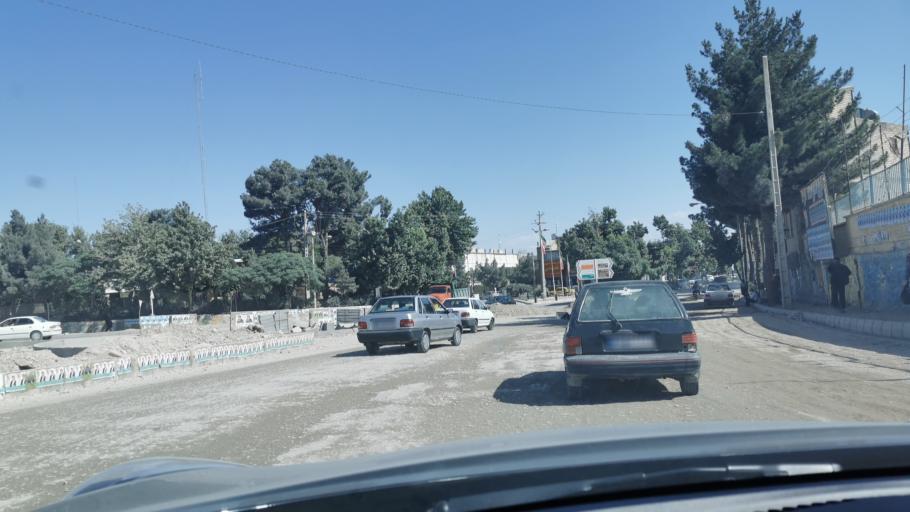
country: IR
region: Razavi Khorasan
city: Chenaran
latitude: 36.6408
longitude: 59.1187
